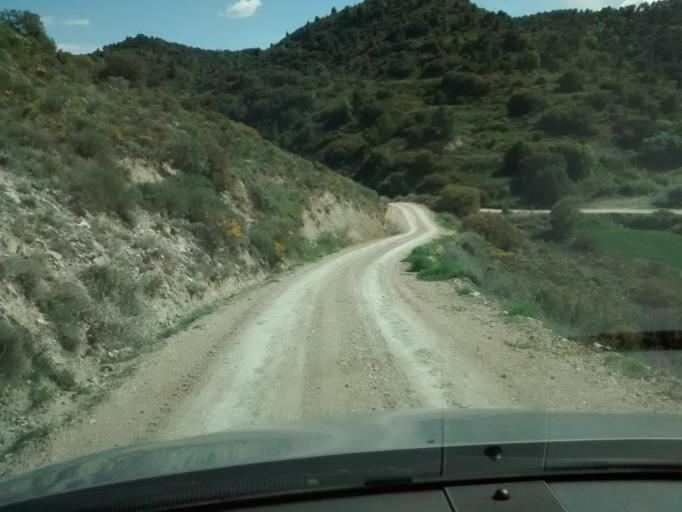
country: ES
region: Aragon
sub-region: Provincia de Huesca
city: Alcubierre
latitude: 41.8164
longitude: -0.5090
